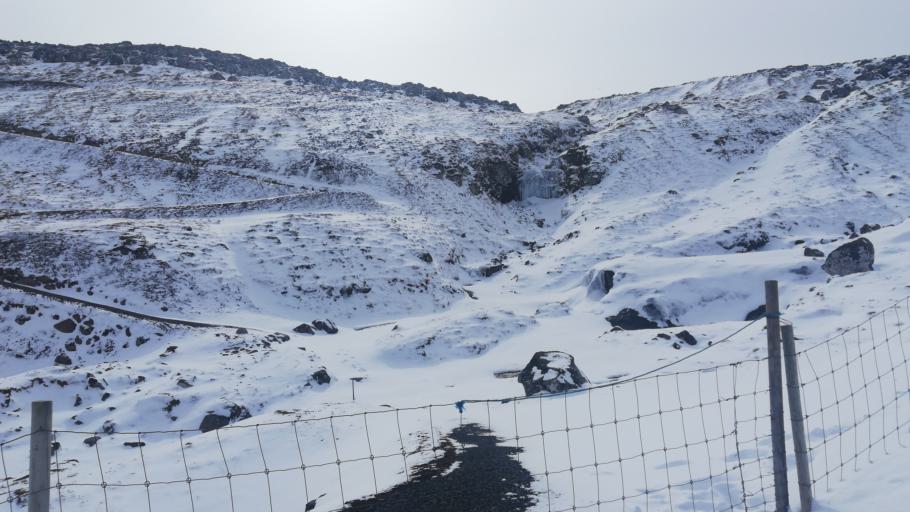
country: FO
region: Streymoy
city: Hoyvik
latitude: 62.0320
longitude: -6.8101
